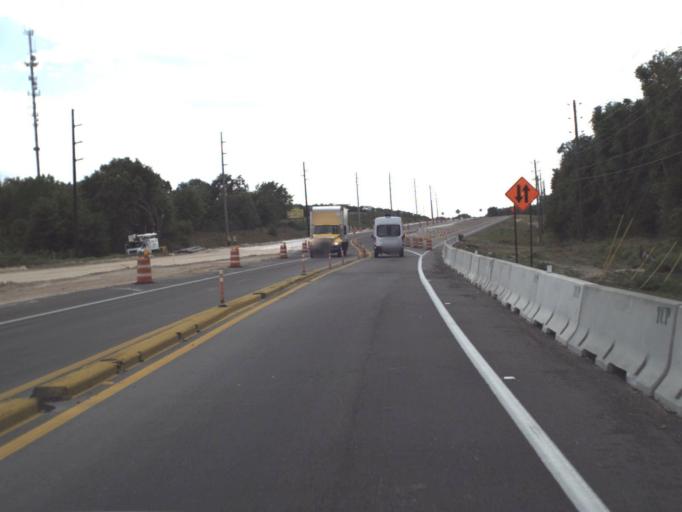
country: US
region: Florida
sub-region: Lake County
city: Clermont
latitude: 28.4729
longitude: -81.7161
